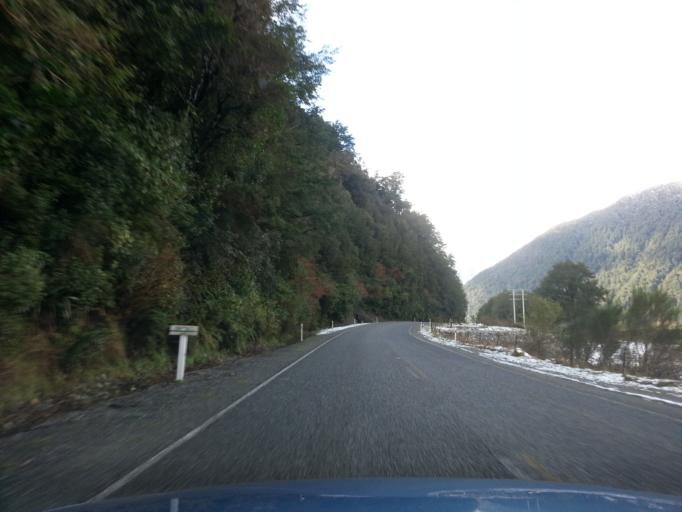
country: NZ
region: West Coast
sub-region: Grey District
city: Greymouth
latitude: -42.7821
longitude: 171.6094
